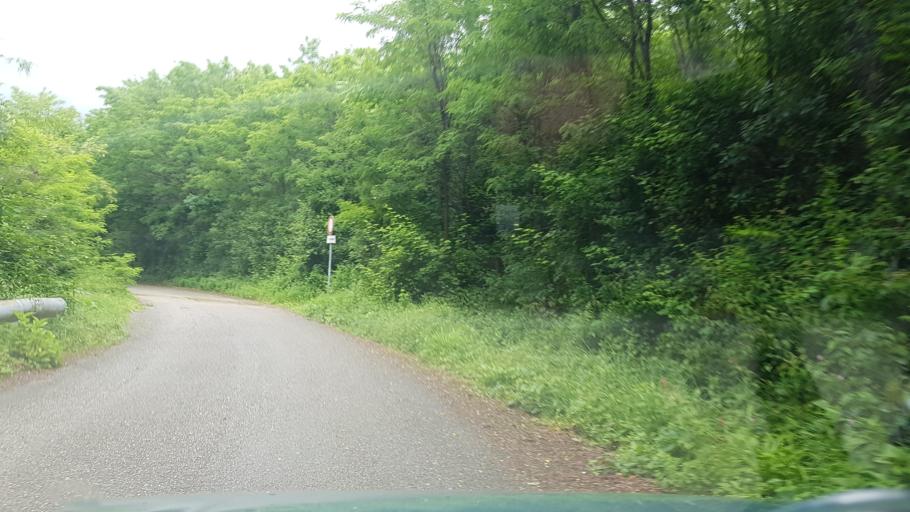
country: IT
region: Friuli Venezia Giulia
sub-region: Provincia di Gorizia
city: San Floriano del Collio
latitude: 45.9490
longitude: 13.5896
